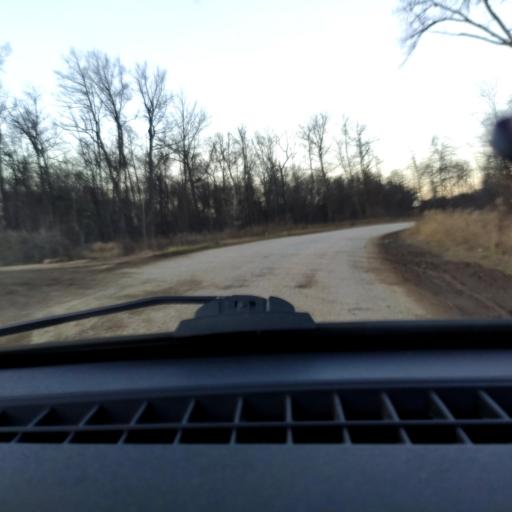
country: RU
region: Bashkortostan
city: Ufa
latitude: 54.7265
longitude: 56.0898
